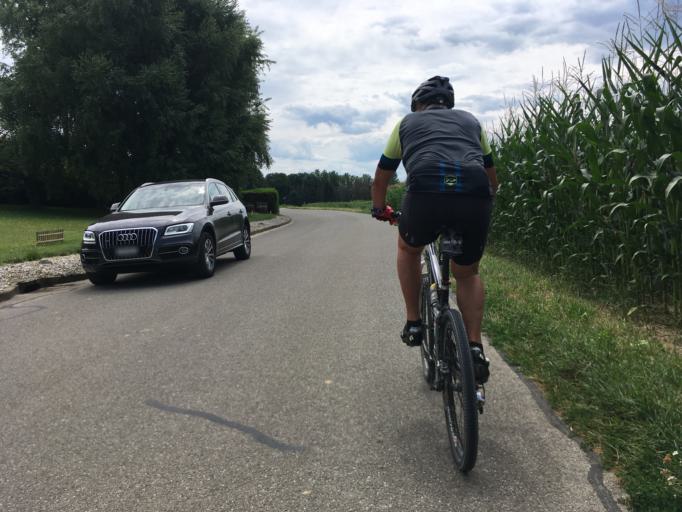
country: CH
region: Fribourg
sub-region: Broye District
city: Estavayer-le-Lac
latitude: 46.8709
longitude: 6.8815
